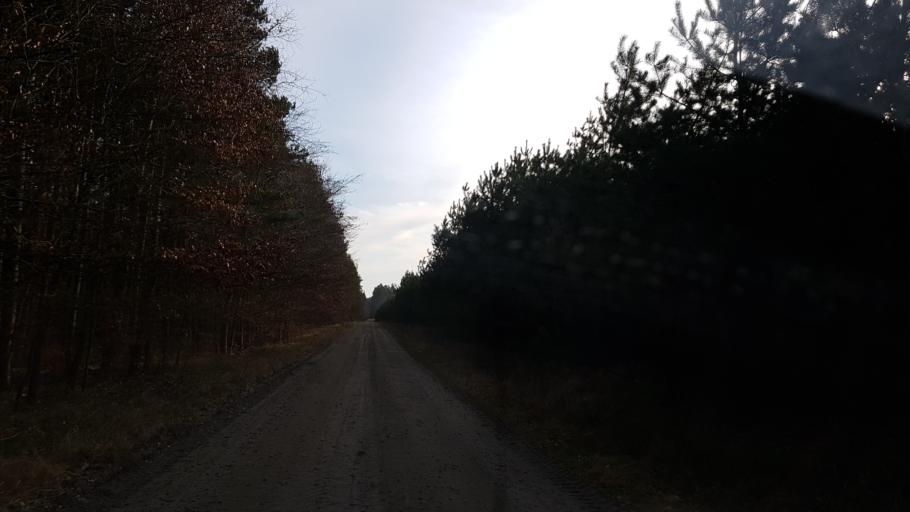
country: PL
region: West Pomeranian Voivodeship
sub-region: Powiat choszczenski
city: Pelczyce
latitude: 52.9294
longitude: 15.3654
